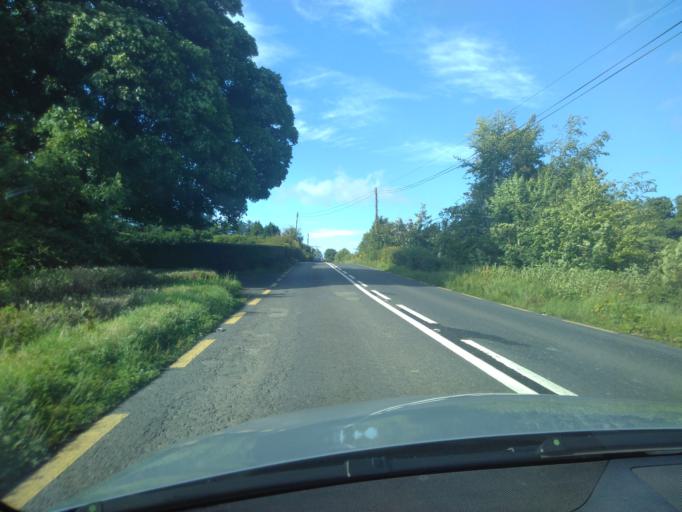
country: IE
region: Ulster
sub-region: County Donegal
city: Ballybofey
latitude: 54.8187
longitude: -7.7569
